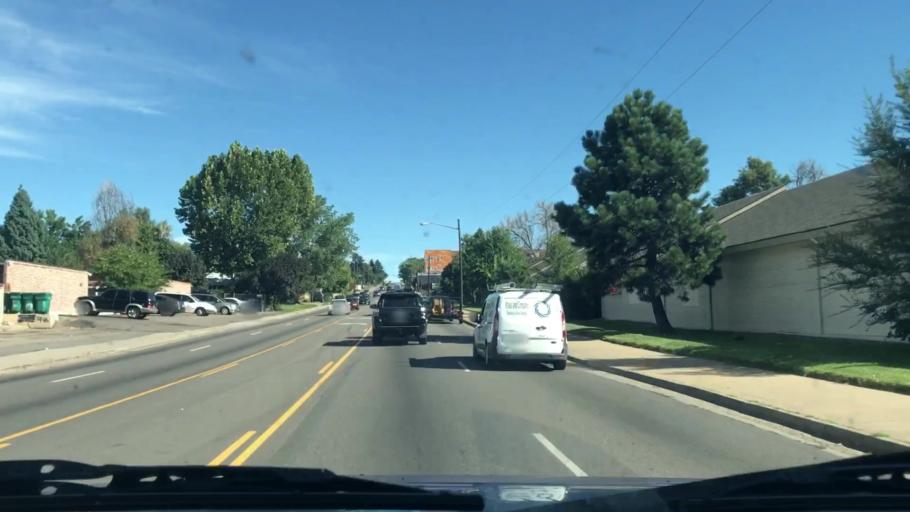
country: US
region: Colorado
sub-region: Jefferson County
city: Edgewater
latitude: 39.7558
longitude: -105.0532
